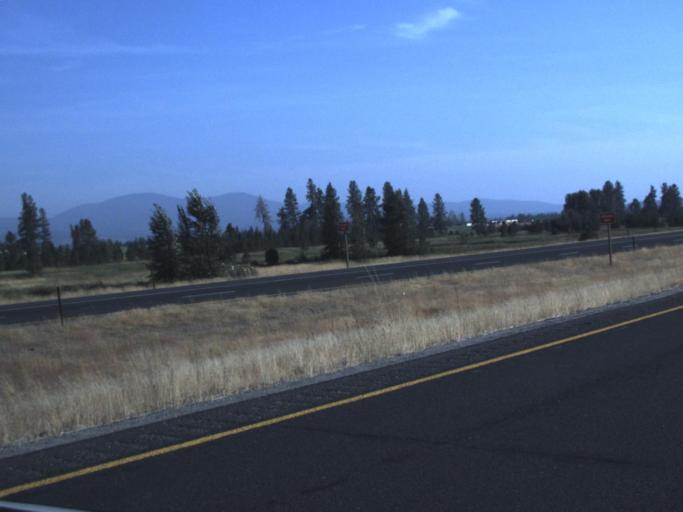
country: US
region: Washington
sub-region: Spokane County
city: Deer Park
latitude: 48.0490
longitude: -117.3440
